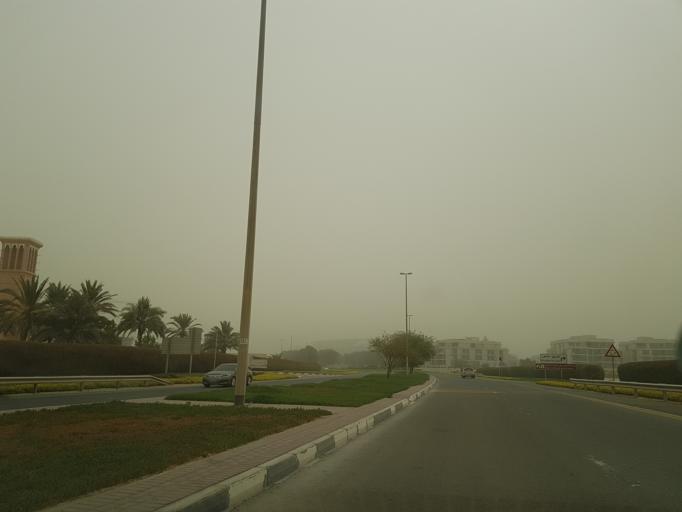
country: AE
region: Dubai
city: Dubai
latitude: 25.1512
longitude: 55.2904
